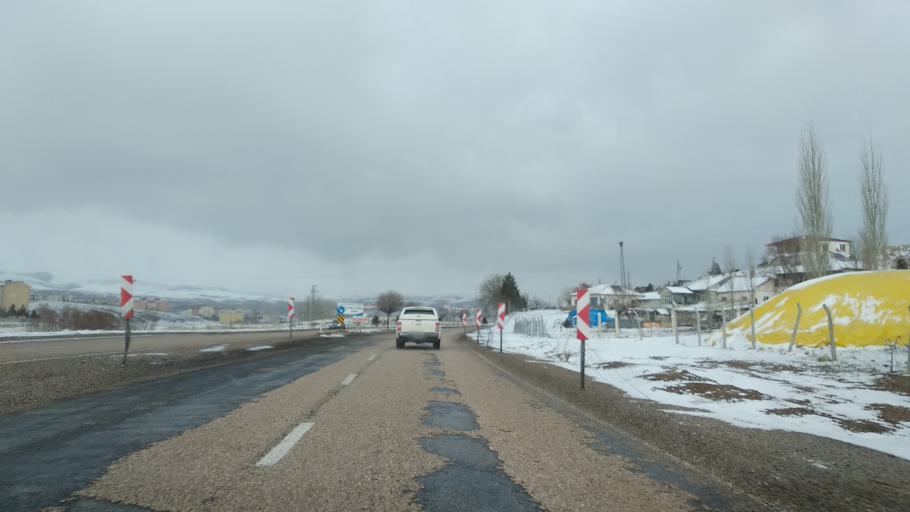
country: TR
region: Kayseri
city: Pinarbasi
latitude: 38.7090
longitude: 36.3764
